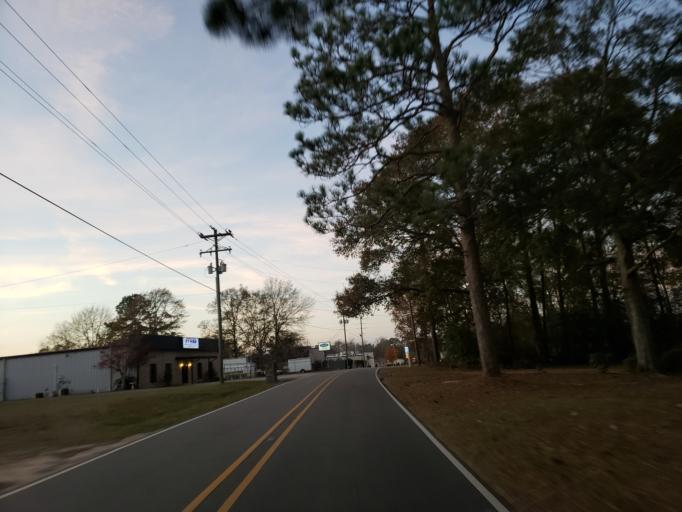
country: US
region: Mississippi
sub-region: Lamar County
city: West Hattiesburg
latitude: 31.2546
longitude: -89.3376
